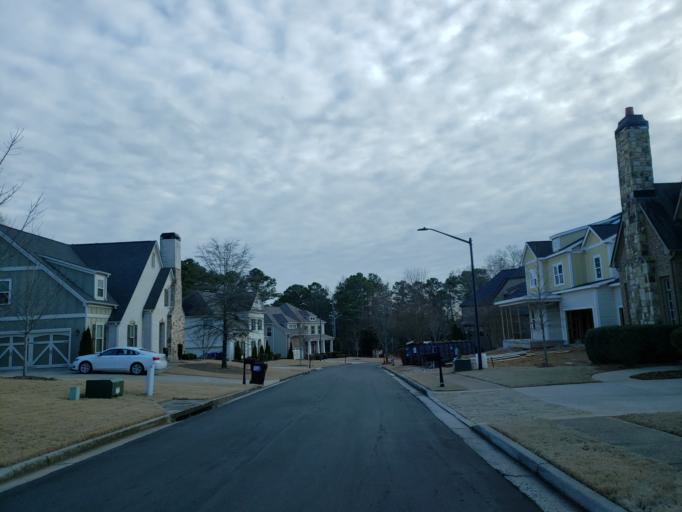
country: US
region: Georgia
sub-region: Cherokee County
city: Woodstock
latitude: 34.0709
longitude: -84.5465
